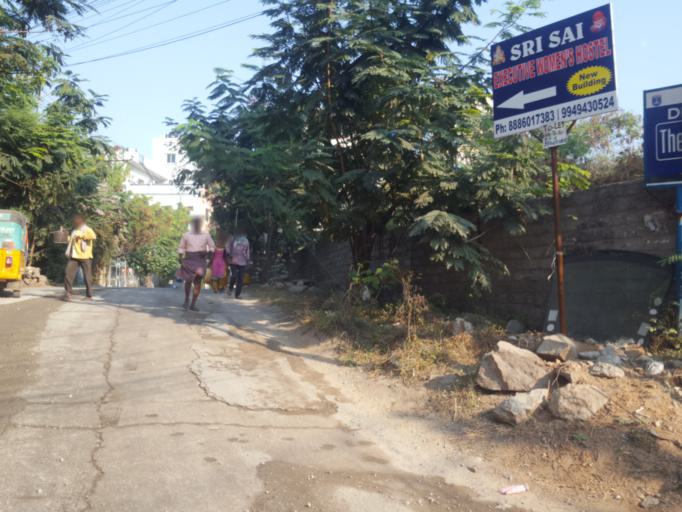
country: IN
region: Telangana
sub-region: Rangareddi
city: Kukatpalli
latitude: 17.4443
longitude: 78.3588
